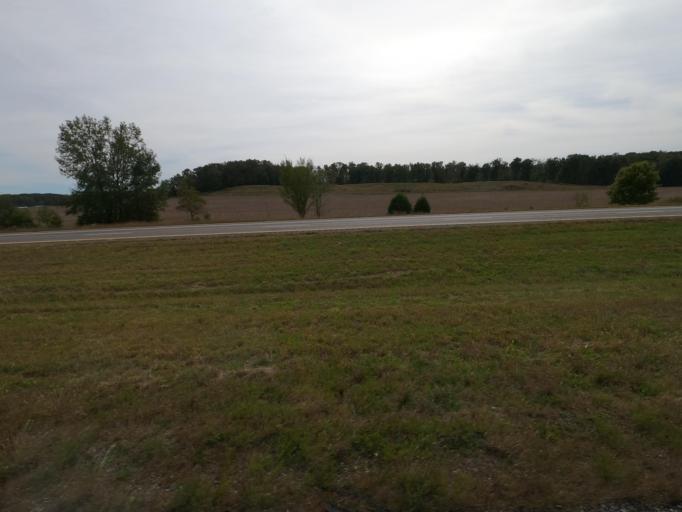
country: US
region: Tennessee
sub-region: Henderson County
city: Lexington
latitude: 35.7866
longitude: -88.4017
